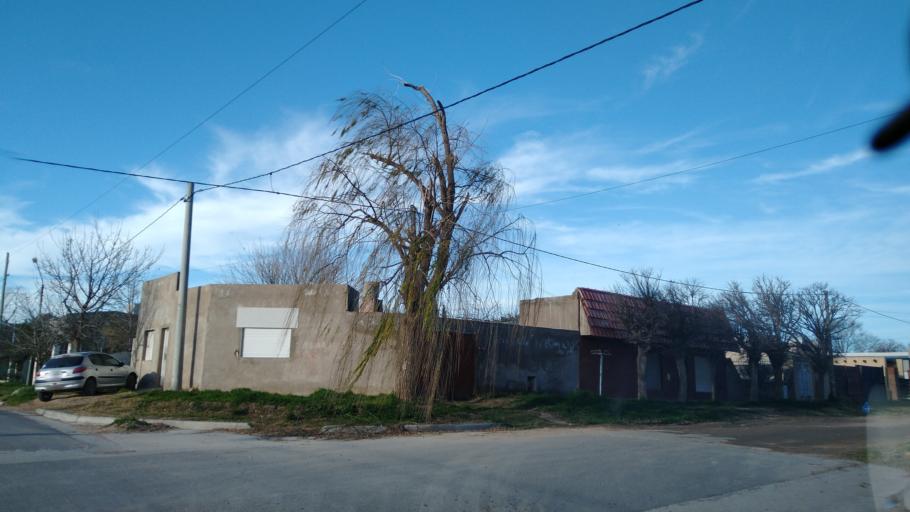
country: AR
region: Buenos Aires
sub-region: Partido de Bahia Blanca
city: Bahia Blanca
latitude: -38.7013
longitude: -62.2104
